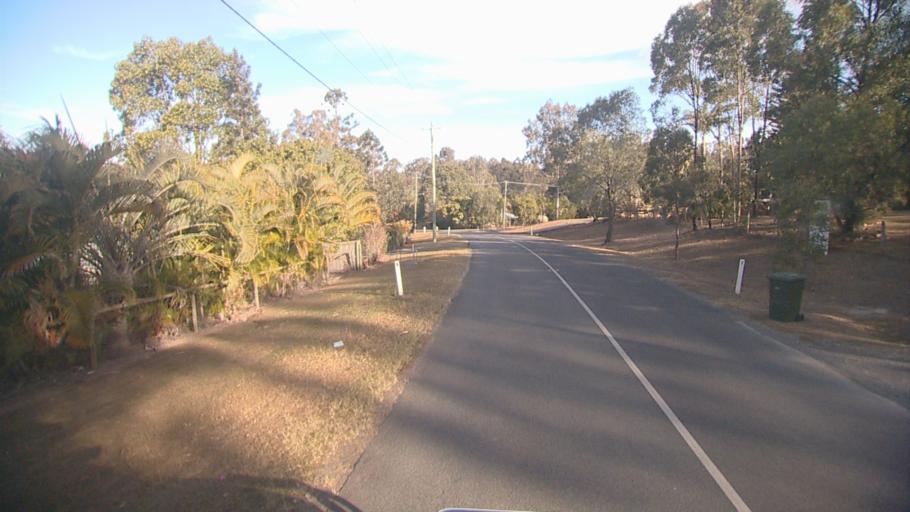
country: AU
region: Queensland
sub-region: Logan
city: Cedar Vale
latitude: -27.8784
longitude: 153.0104
